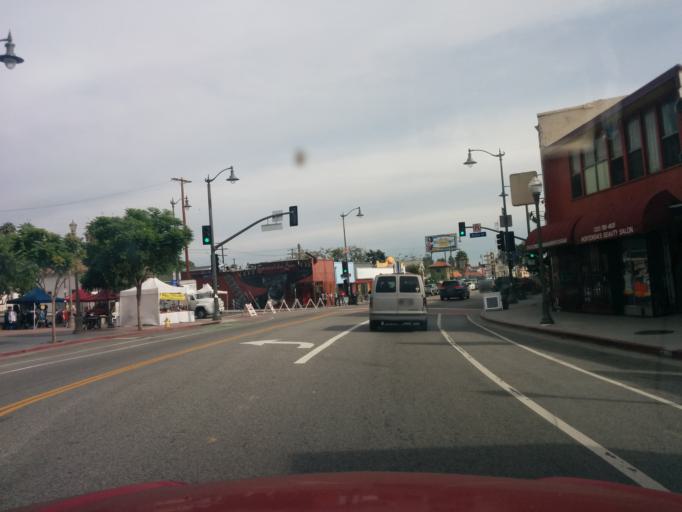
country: US
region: California
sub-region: Los Angeles County
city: Boyle Heights
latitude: 34.0471
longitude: -118.2192
